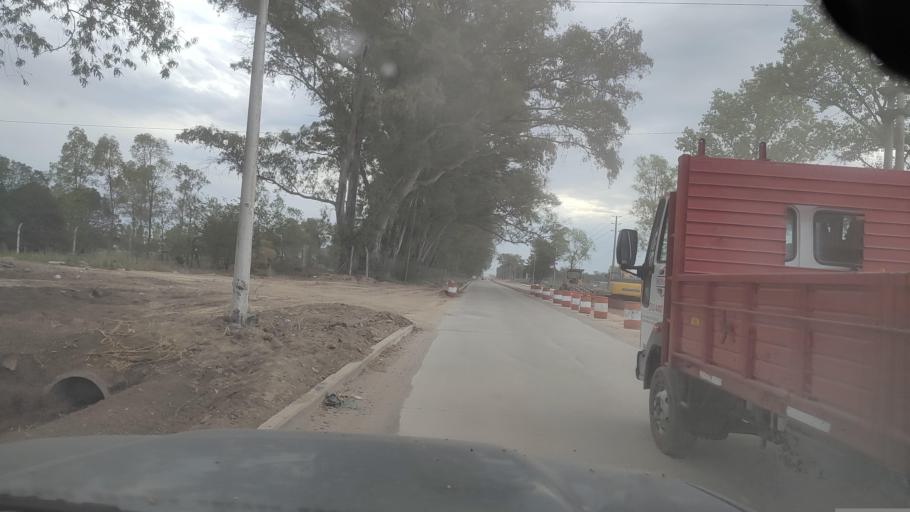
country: AR
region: Buenos Aires
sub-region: Partido de Lujan
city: Lujan
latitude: -34.5504
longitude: -59.0875
